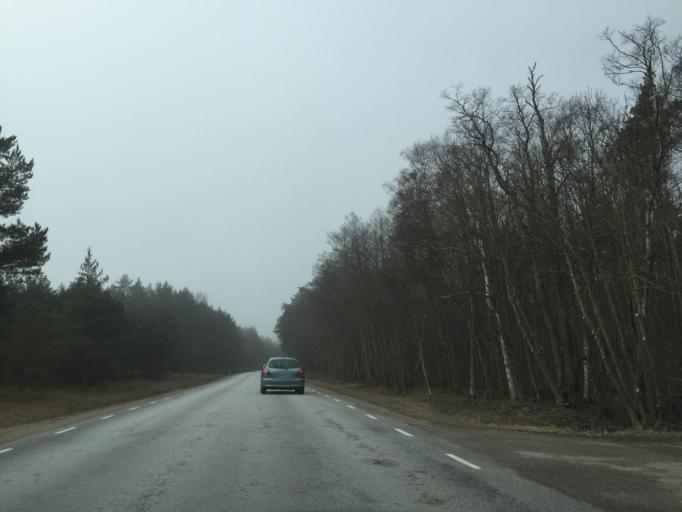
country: EE
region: Saare
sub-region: Kuressaare linn
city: Kuressaare
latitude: 58.2079
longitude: 22.3035
